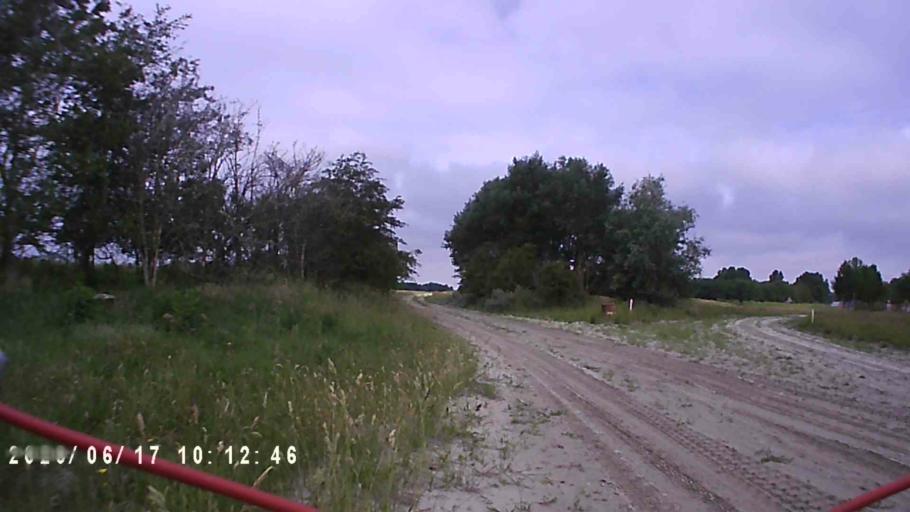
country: NL
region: Groningen
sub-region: Gemeente De Marne
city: Ulrum
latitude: 53.3828
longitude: 6.2656
